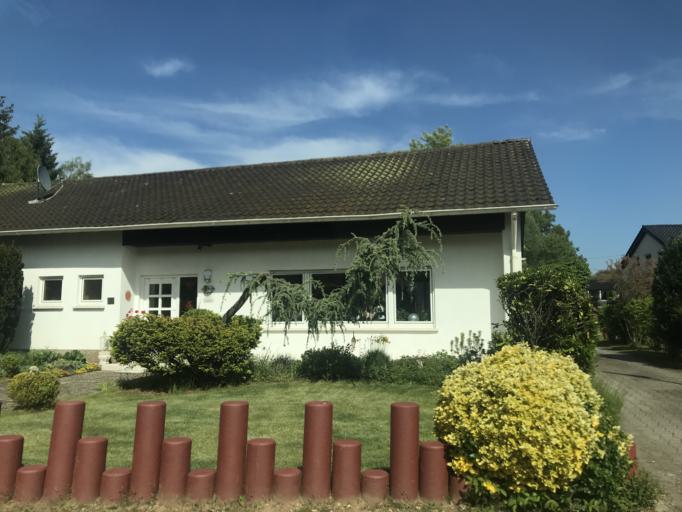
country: DE
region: Saarland
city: Losheim
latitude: 49.4494
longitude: 6.7603
